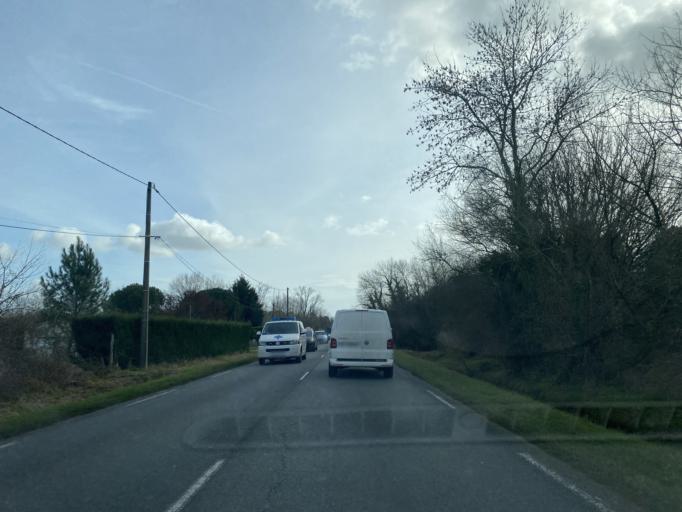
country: FR
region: Aquitaine
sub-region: Departement de la Gironde
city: Le Taillan-Medoc
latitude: 44.9254
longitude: -0.6768
